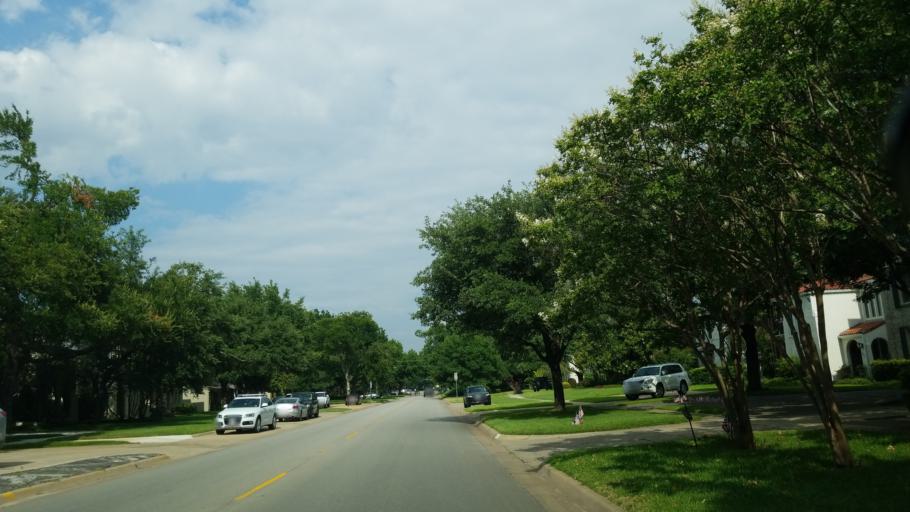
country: US
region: Texas
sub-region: Dallas County
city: University Park
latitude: 32.8453
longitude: -96.8083
